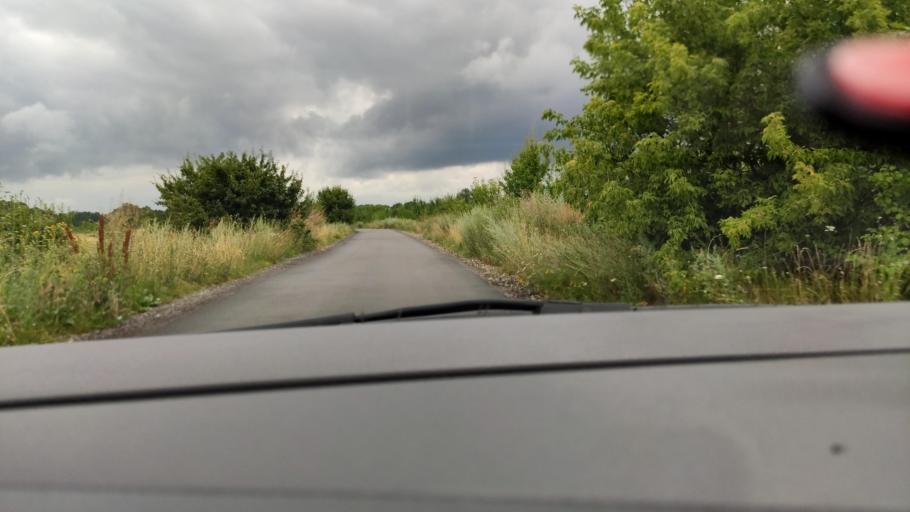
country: RU
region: Voronezj
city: Ramon'
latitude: 51.9005
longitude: 39.3502
